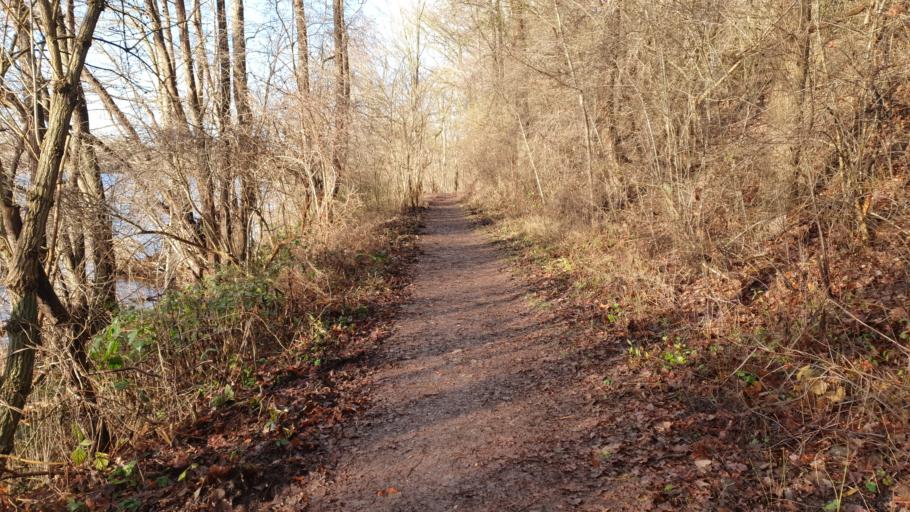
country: DE
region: Mecklenburg-Vorpommern
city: Neumuehle
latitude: 53.6324
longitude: 11.3539
